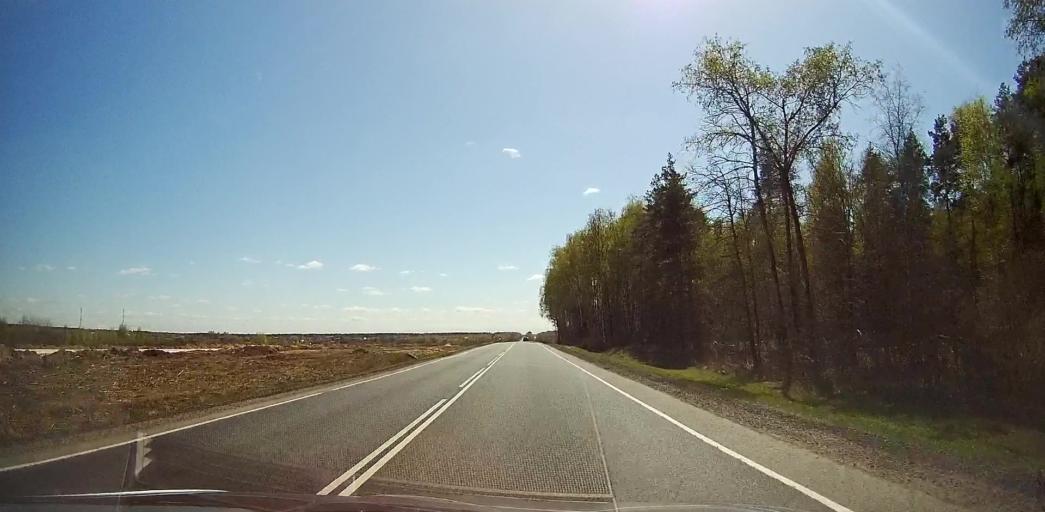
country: RU
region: Moskovskaya
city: Gzhel'
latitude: 55.5869
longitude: 38.3846
